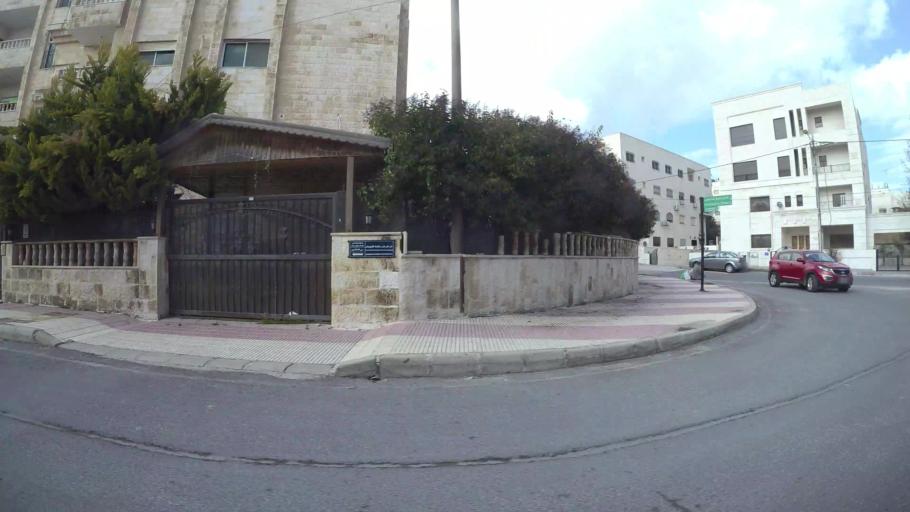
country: JO
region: Amman
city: Wadi as Sir
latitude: 31.9831
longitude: 35.8501
